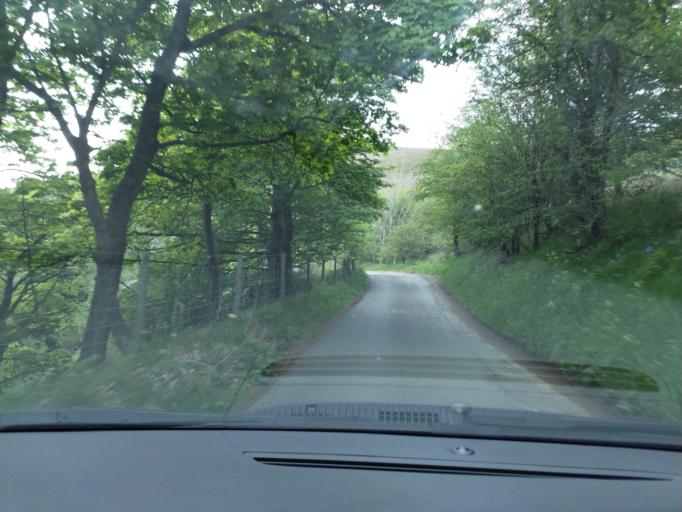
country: GB
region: England
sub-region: Derbyshire
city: Hathersage
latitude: 53.3526
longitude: -1.6704
